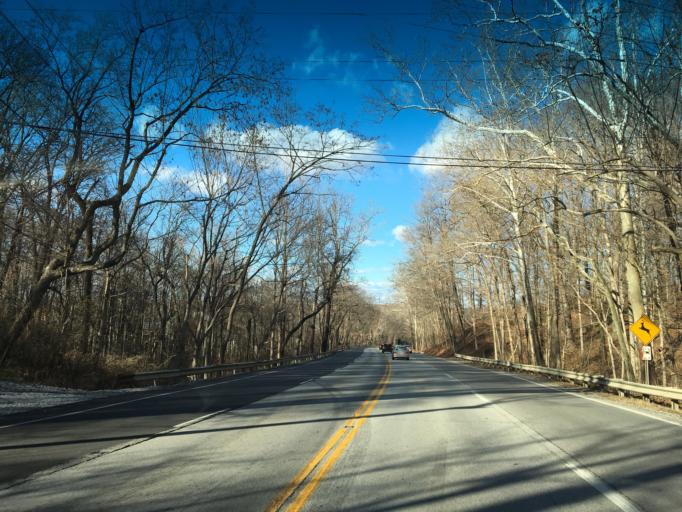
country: US
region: Kentucky
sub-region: Jefferson County
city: Prospect
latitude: 38.3276
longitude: -85.6218
